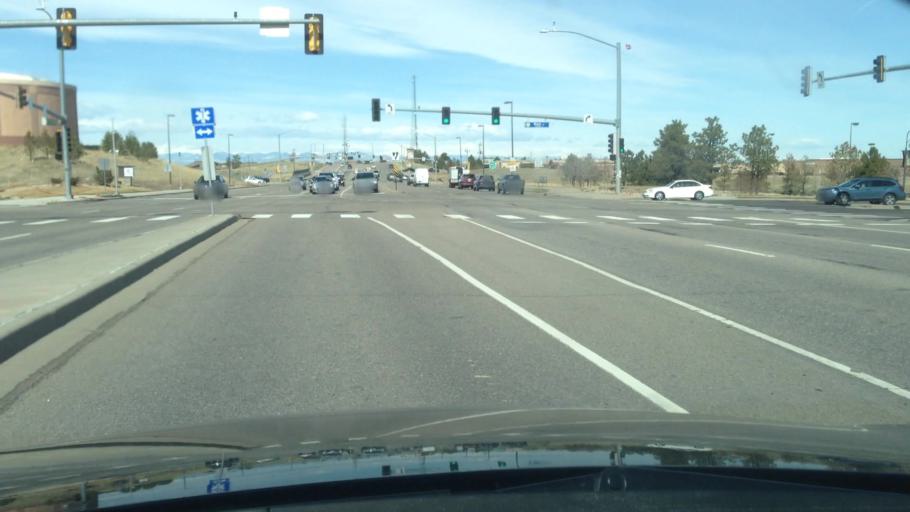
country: US
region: Colorado
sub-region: Douglas County
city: Parker
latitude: 39.5997
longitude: -104.7108
